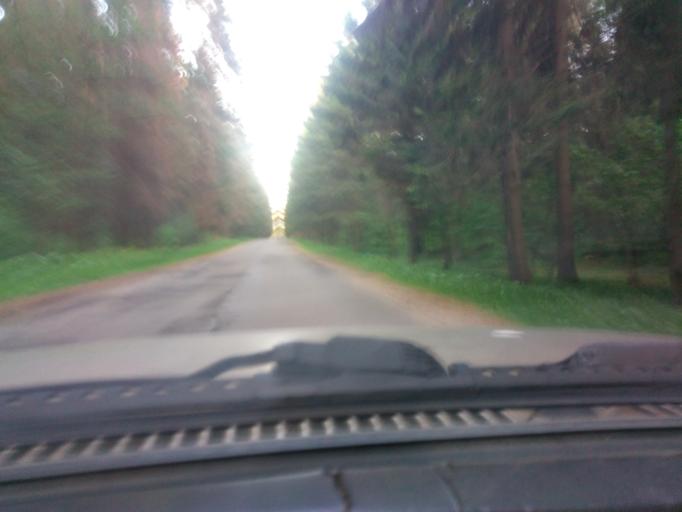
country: BY
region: Mogilev
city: Mahilyow
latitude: 53.9322
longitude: 30.2966
